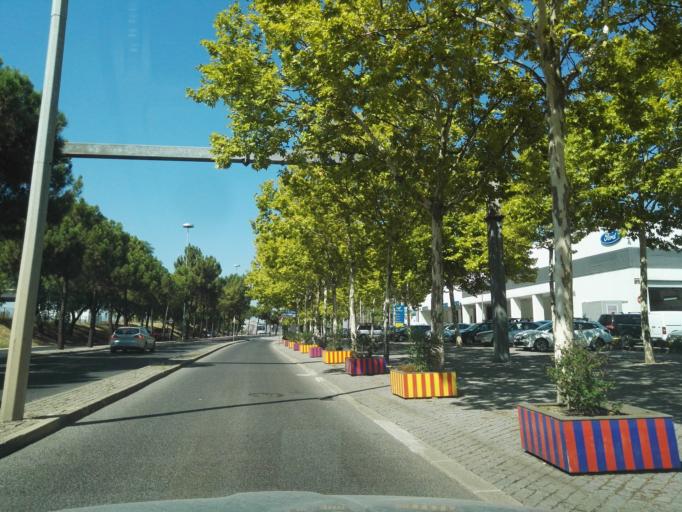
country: PT
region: Lisbon
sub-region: Loures
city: Moscavide
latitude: 38.7839
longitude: -9.0999
